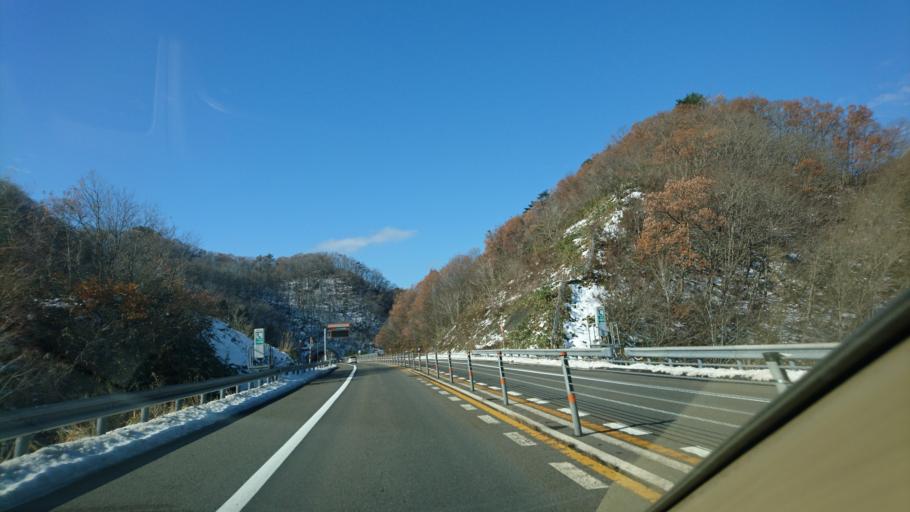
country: JP
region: Akita
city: Yokotemachi
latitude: 39.3141
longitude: 140.7697
